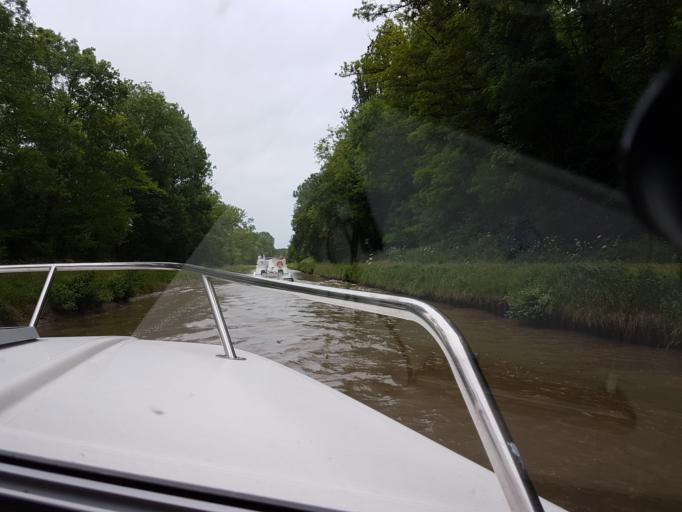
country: FR
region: Bourgogne
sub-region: Departement de la Nievre
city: Clamecy
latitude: 47.4034
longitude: 3.6071
